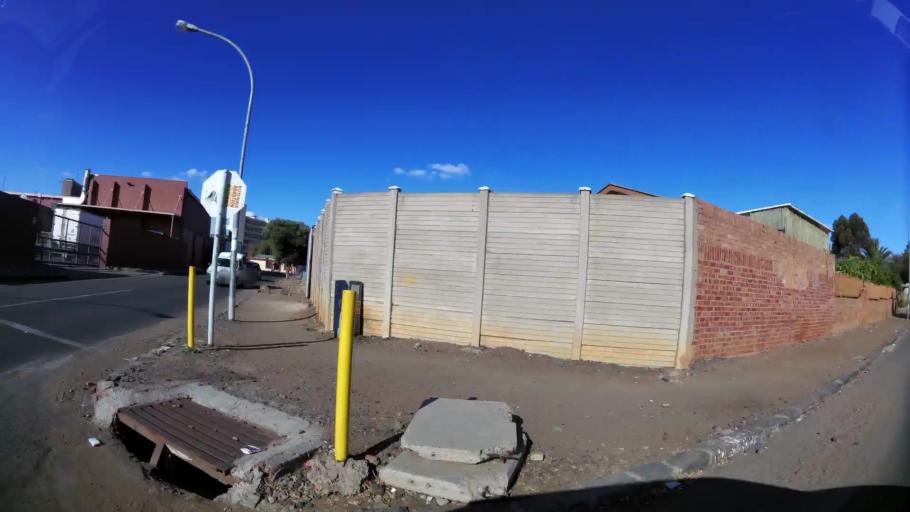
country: ZA
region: Northern Cape
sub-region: Frances Baard District Municipality
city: Kimberley
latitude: -28.7460
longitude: 24.7617
